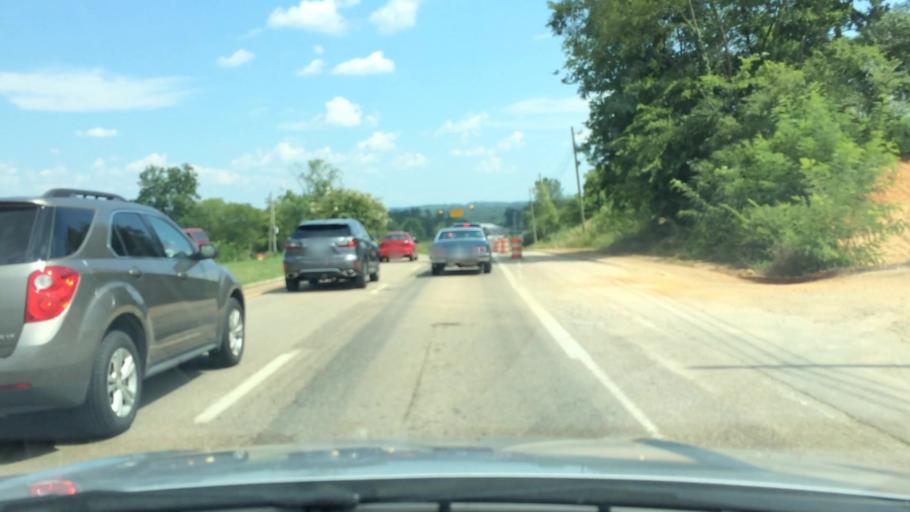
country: US
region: Tennessee
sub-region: Loudon County
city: Lenoir City
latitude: 35.8002
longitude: -84.2589
